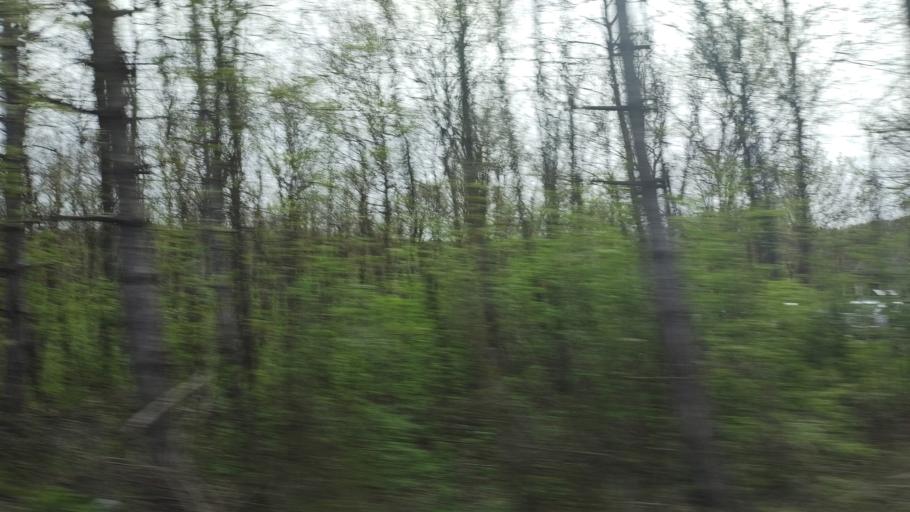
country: RO
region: Constanta
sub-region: Oras Murfatlar
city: Siminoc
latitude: 44.1574
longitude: 28.3810
